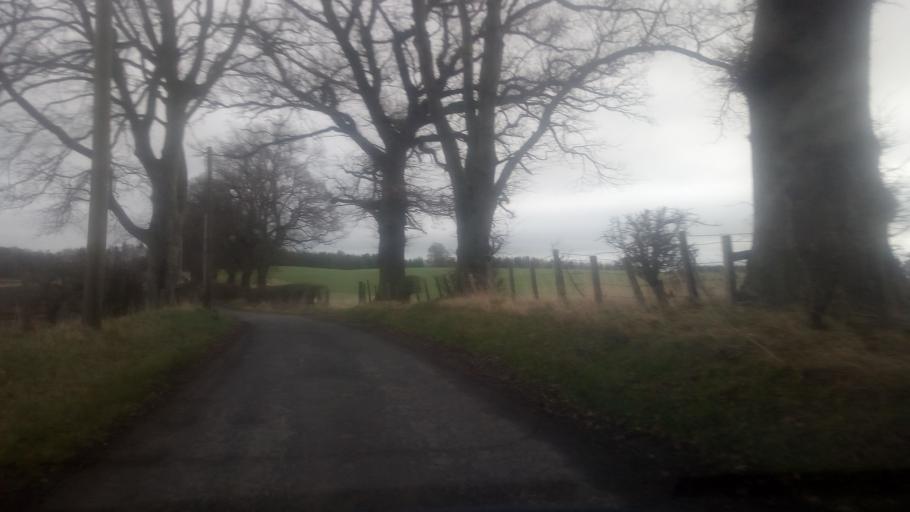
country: GB
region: Scotland
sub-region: The Scottish Borders
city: Jedburgh
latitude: 55.5300
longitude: -2.5072
